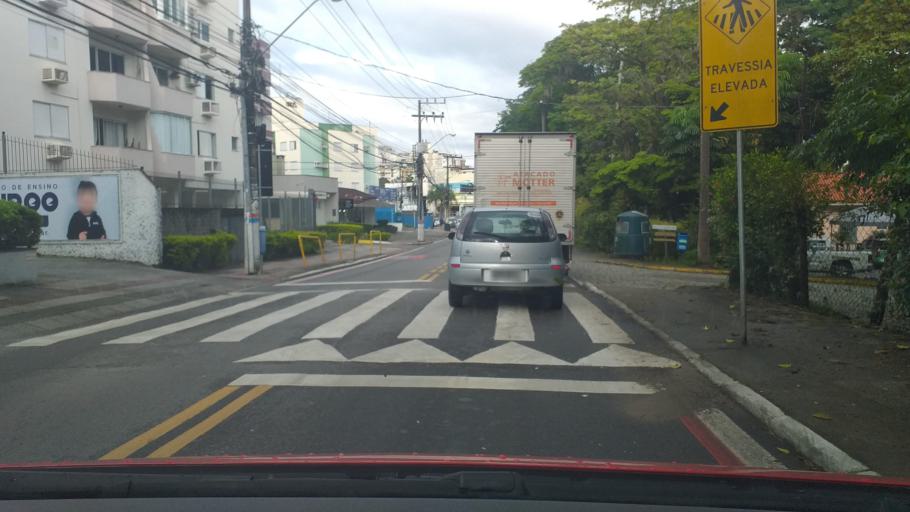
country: BR
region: Santa Catarina
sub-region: Florianopolis
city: Corrego Grande
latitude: -27.5999
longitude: -48.5112
